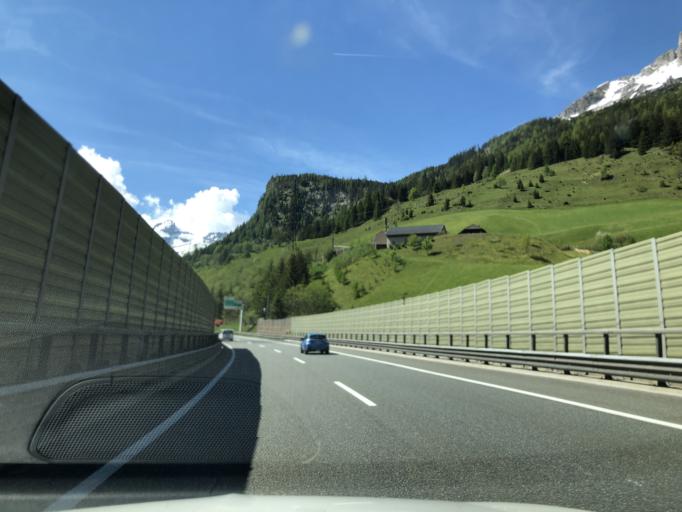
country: AT
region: Salzburg
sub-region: Politischer Bezirk Tamsweg
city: Zederhaus
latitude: 47.1700
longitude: 13.4633
